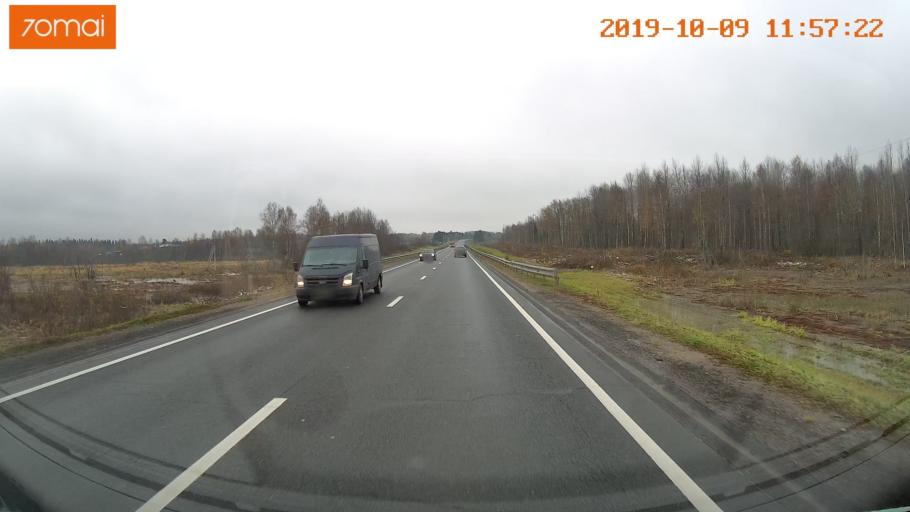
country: RU
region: Vologda
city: Gryazovets
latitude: 58.7332
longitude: 40.2922
